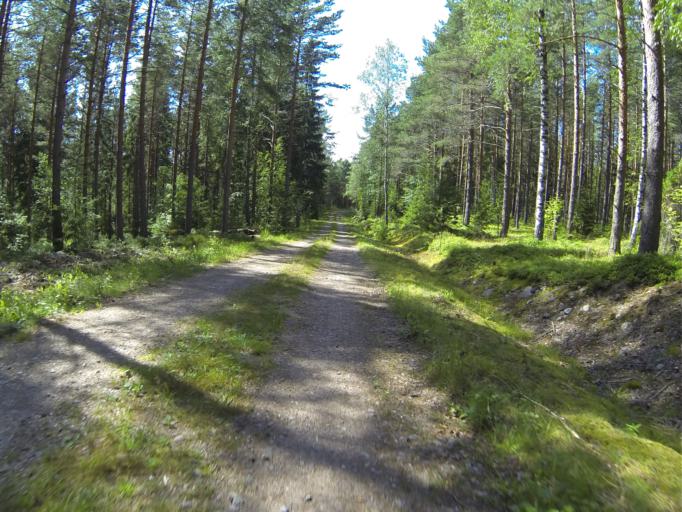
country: FI
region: Varsinais-Suomi
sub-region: Salo
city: Pernioe
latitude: 60.2830
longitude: 23.0647
